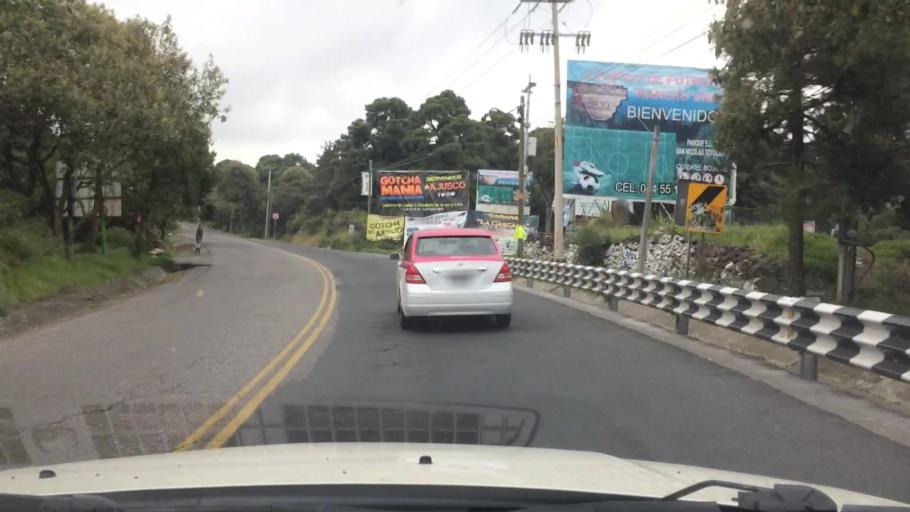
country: MX
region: Mexico City
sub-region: Tlalpan
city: Lomas de Tepemecatl
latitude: 19.2636
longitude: -99.2404
